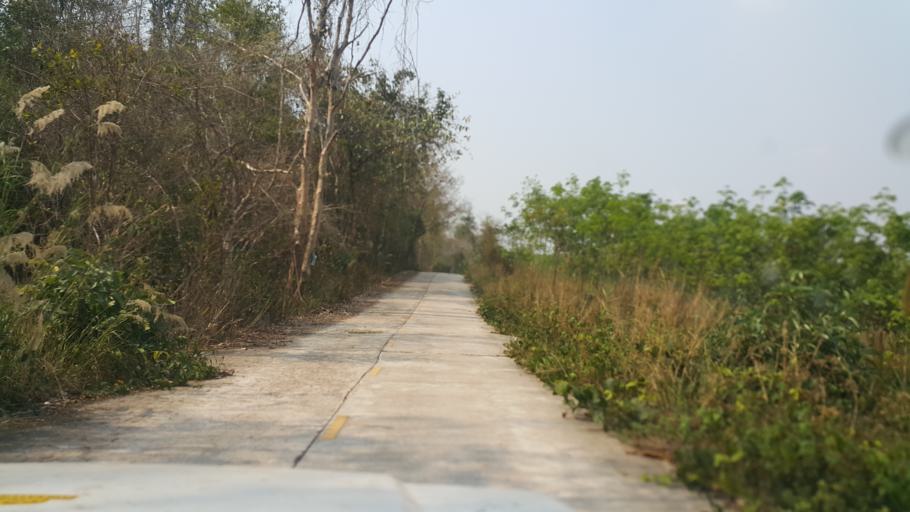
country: TH
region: Nakhon Phanom
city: Ban Phaeng
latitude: 17.9770
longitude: 104.1492
